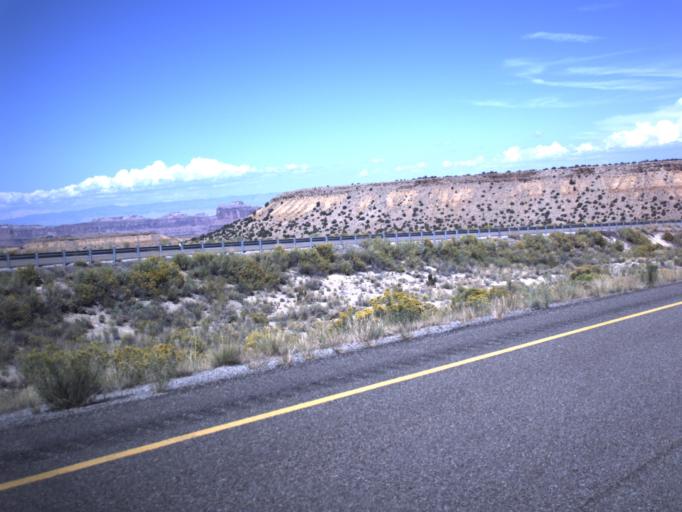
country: US
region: Utah
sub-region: Emery County
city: Castle Dale
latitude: 38.9139
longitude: -110.5196
